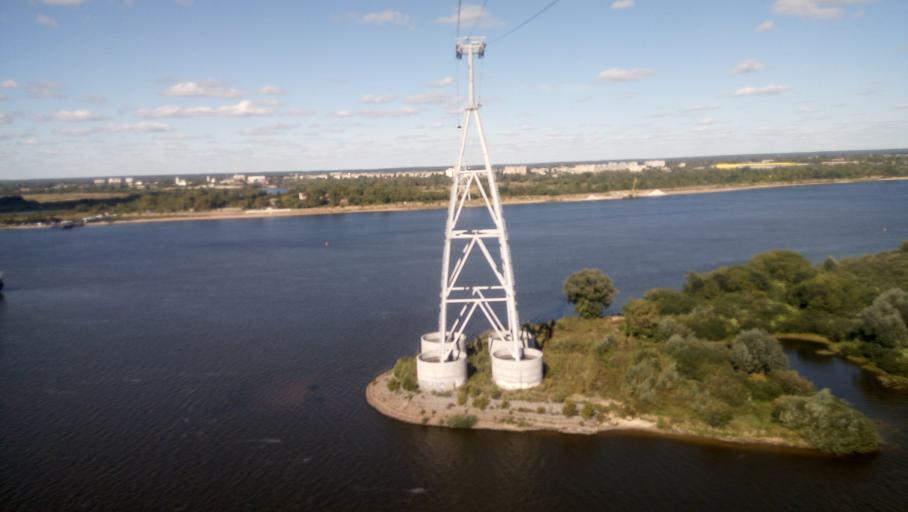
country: RU
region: Nizjnij Novgorod
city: Bor
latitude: 56.3322
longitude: 44.0453
